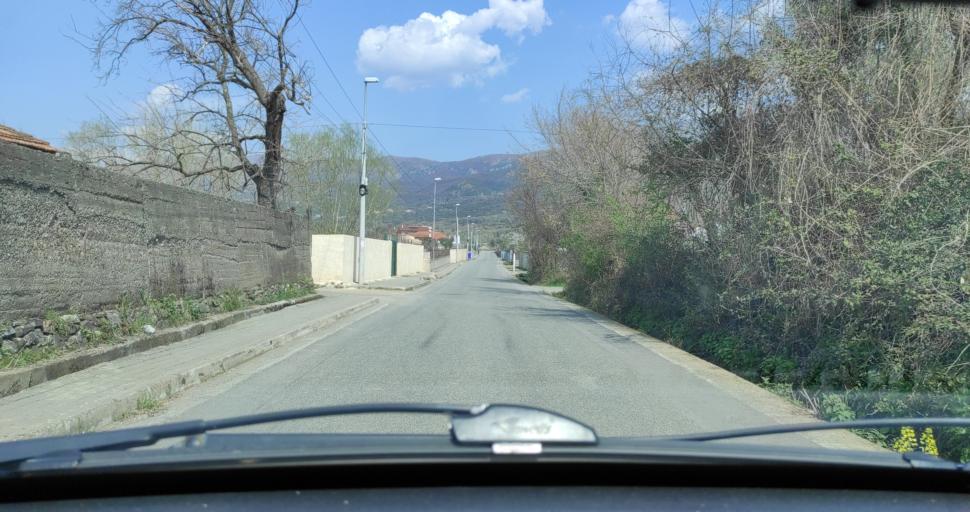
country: AL
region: Lezhe
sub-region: Rrethi i Lezhes
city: Kallmeti i Madh
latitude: 41.8564
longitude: 19.6955
